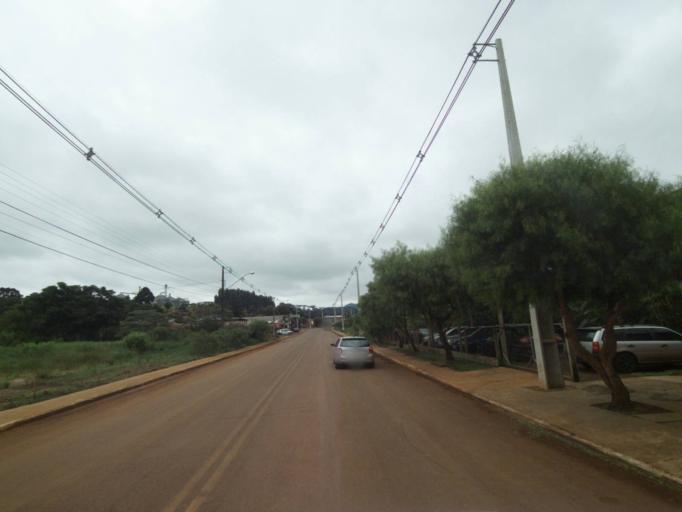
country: BR
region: Parana
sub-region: Pitanga
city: Pitanga
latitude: -24.9332
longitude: -51.8727
